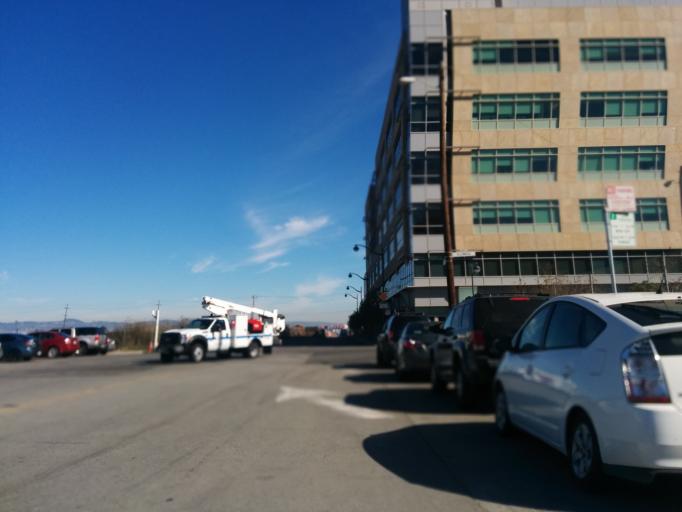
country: US
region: California
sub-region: San Francisco County
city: San Francisco
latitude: 37.7670
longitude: -122.3886
